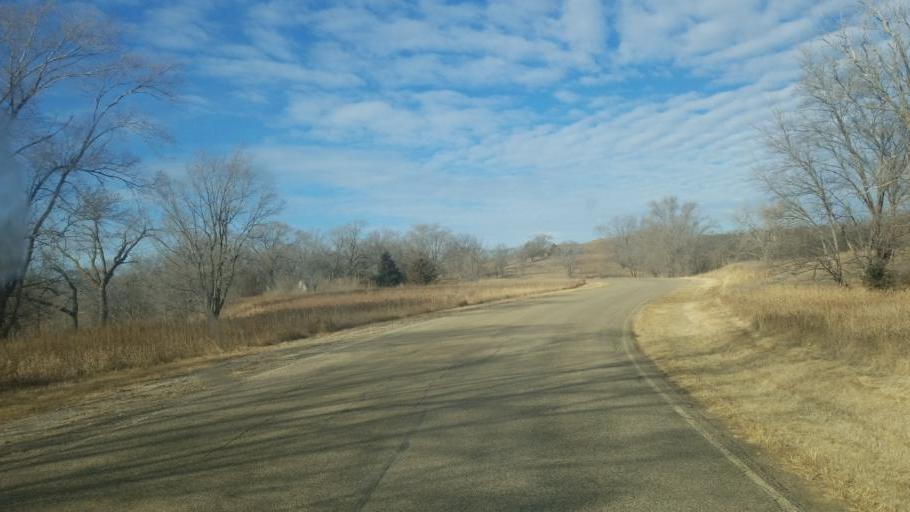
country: US
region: South Dakota
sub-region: Charles Mix County
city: Wagner
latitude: 42.9236
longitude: -98.3895
